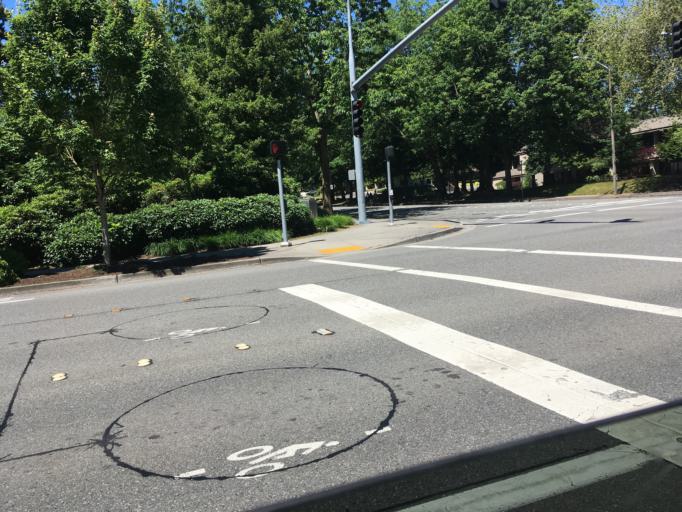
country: US
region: Washington
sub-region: King County
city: Redmond
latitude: 47.6457
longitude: -122.1403
